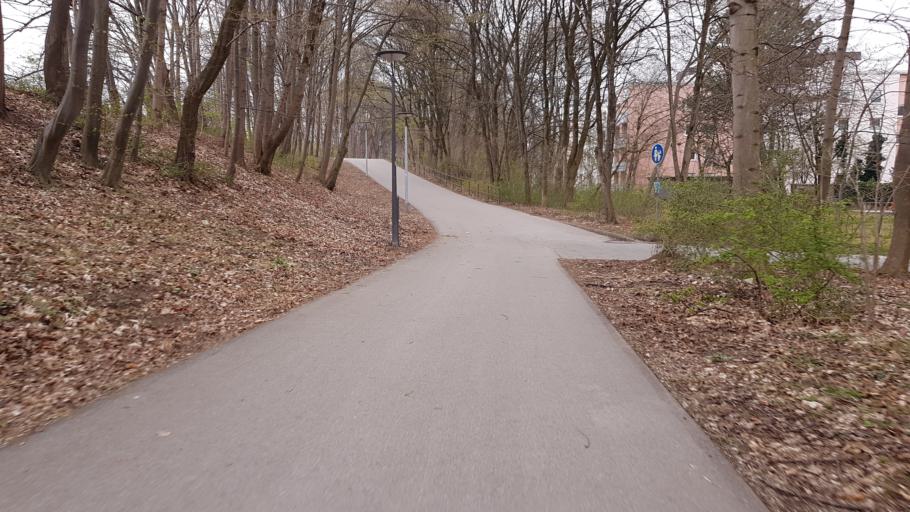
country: DE
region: Bavaria
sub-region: Upper Bavaria
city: Pasing
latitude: 48.1242
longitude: 11.4765
